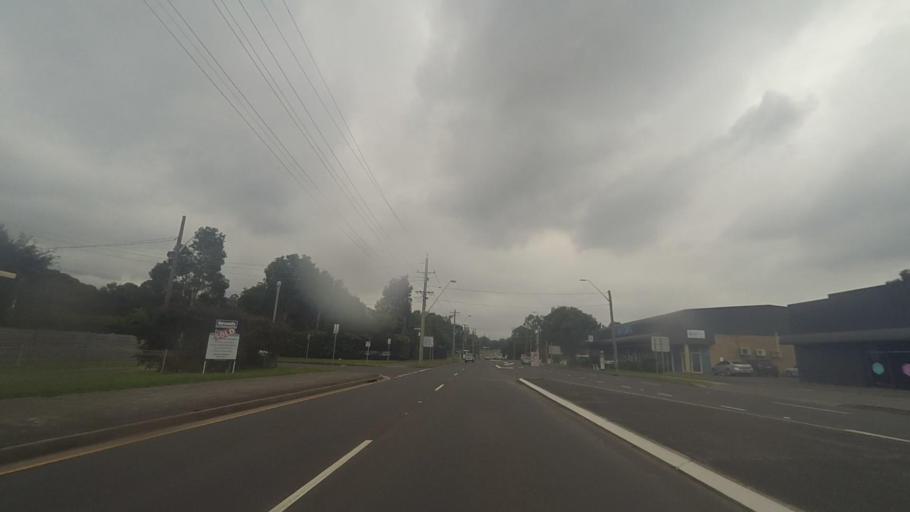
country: AU
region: New South Wales
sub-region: Wollongong
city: Cordeaux Heights
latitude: -34.4493
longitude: 150.8497
